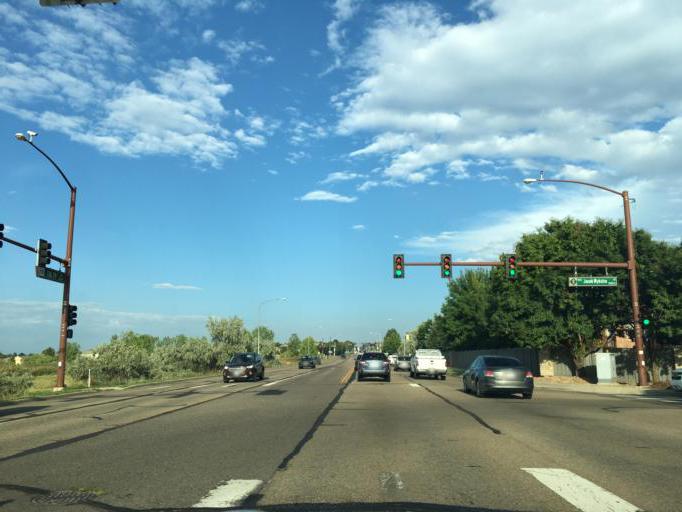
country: US
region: Colorado
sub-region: Adams County
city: Northglenn
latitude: 39.9428
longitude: -104.9634
